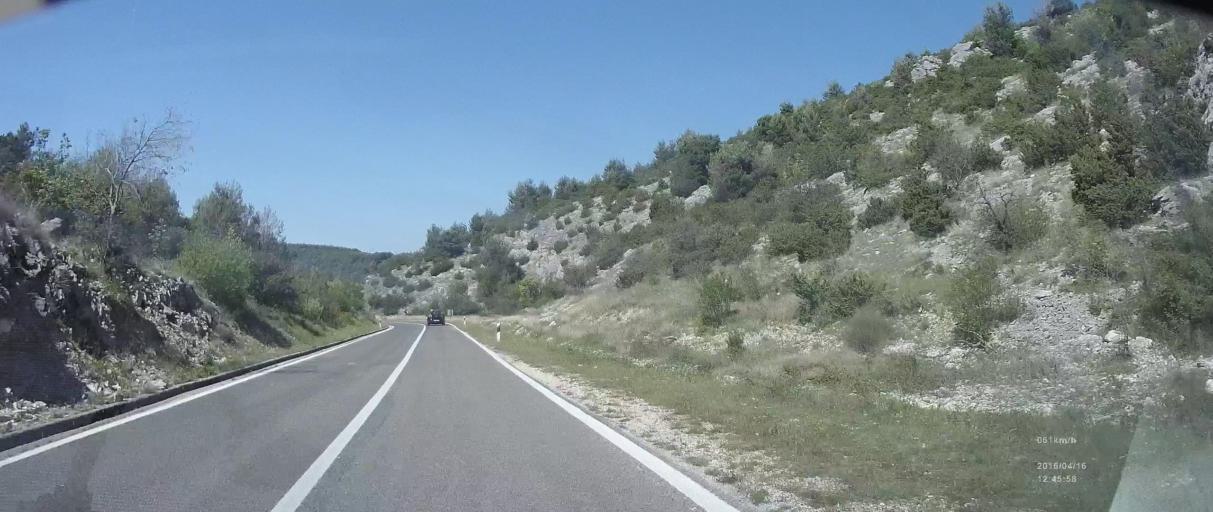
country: HR
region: Sibensko-Kniniska
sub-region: Grad Sibenik
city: Brodarica
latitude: 43.6525
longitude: 16.0596
